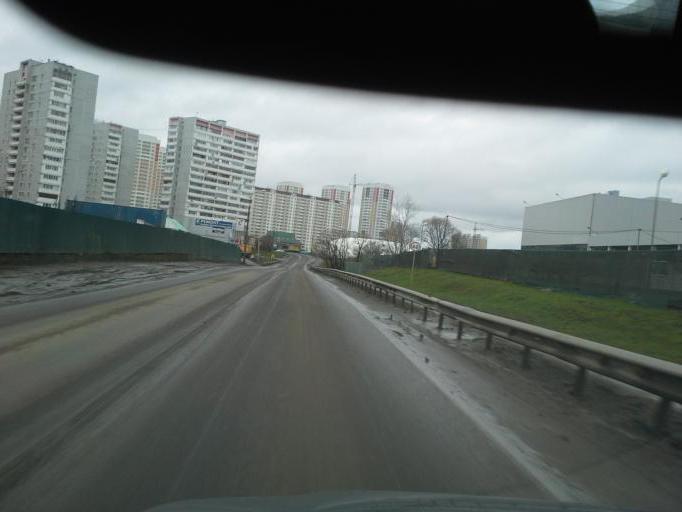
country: RU
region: Moskovskaya
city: Moskovskiy
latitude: 55.5953
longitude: 37.3524
